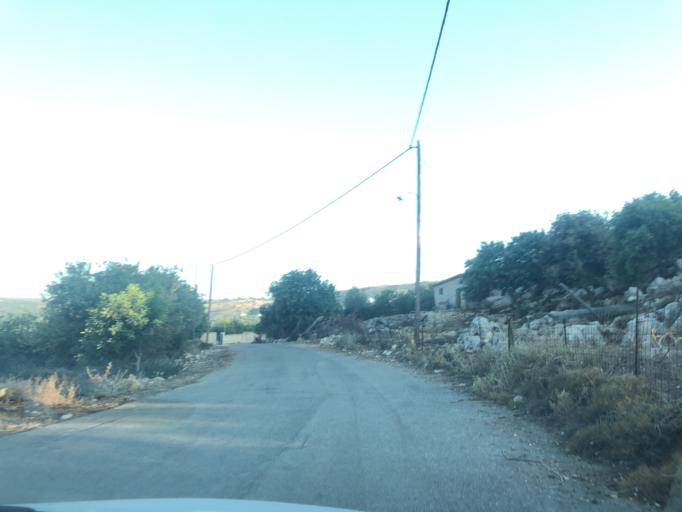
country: GR
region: Crete
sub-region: Nomos Rethymnis
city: Atsipopoulon
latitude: 35.3572
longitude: 24.3970
